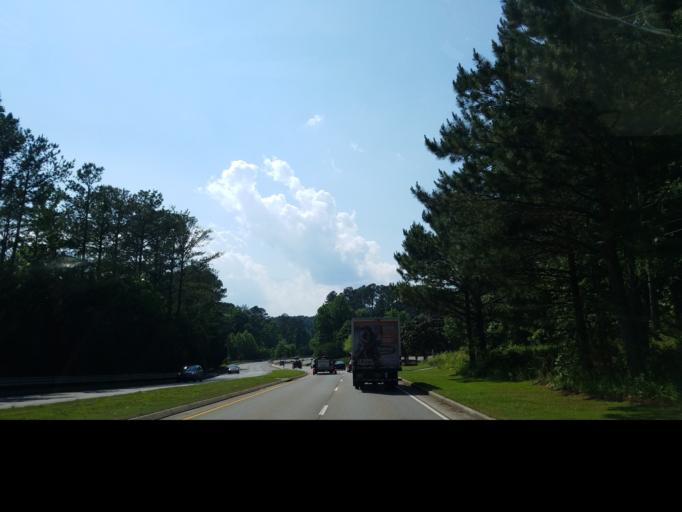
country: US
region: Georgia
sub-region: Cherokee County
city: Holly Springs
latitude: 34.1604
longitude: -84.5340
